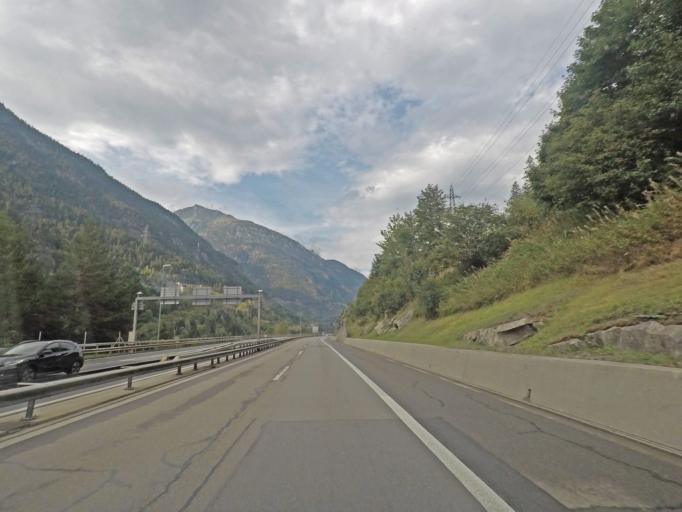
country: CH
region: Uri
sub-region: Uri
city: Andermatt
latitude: 46.6902
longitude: 8.5952
